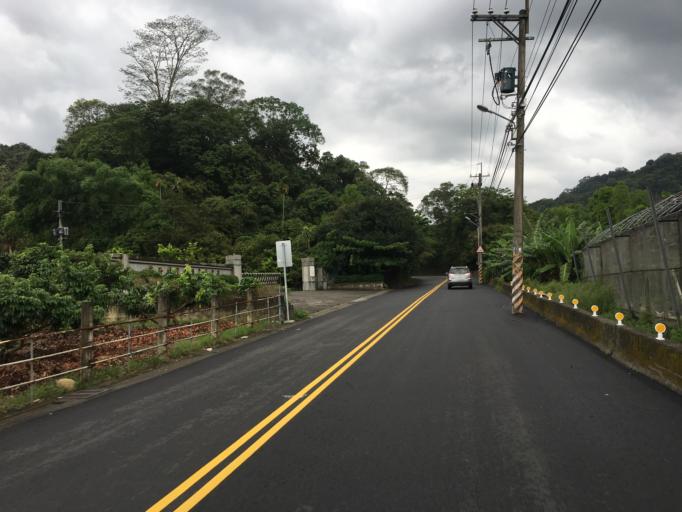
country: TW
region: Taiwan
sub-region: Taichung City
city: Taichung
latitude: 24.0655
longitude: 120.7357
